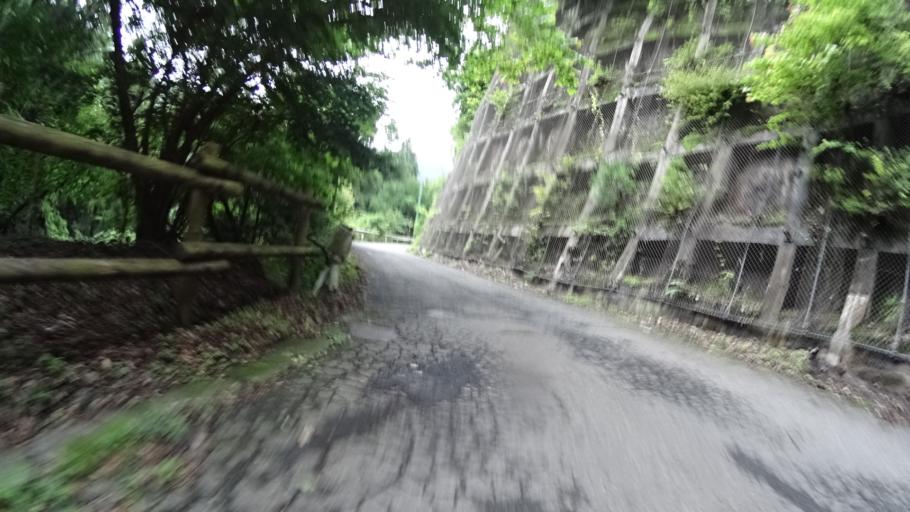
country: JP
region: Kanagawa
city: Hadano
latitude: 35.4761
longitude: 139.2101
